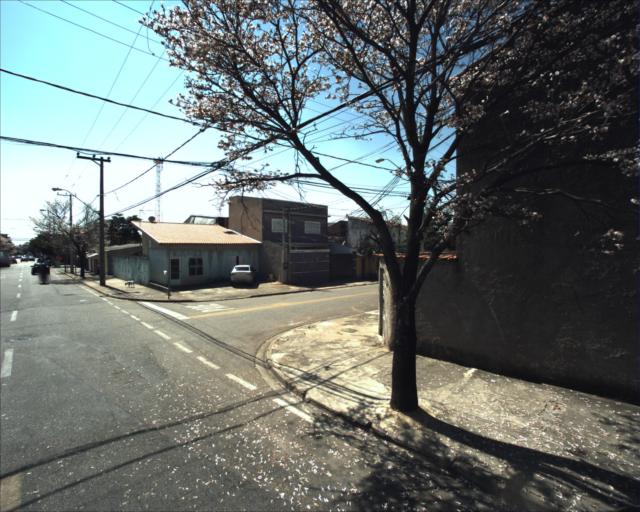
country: BR
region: Sao Paulo
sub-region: Sorocaba
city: Sorocaba
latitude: -23.5046
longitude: -47.5169
